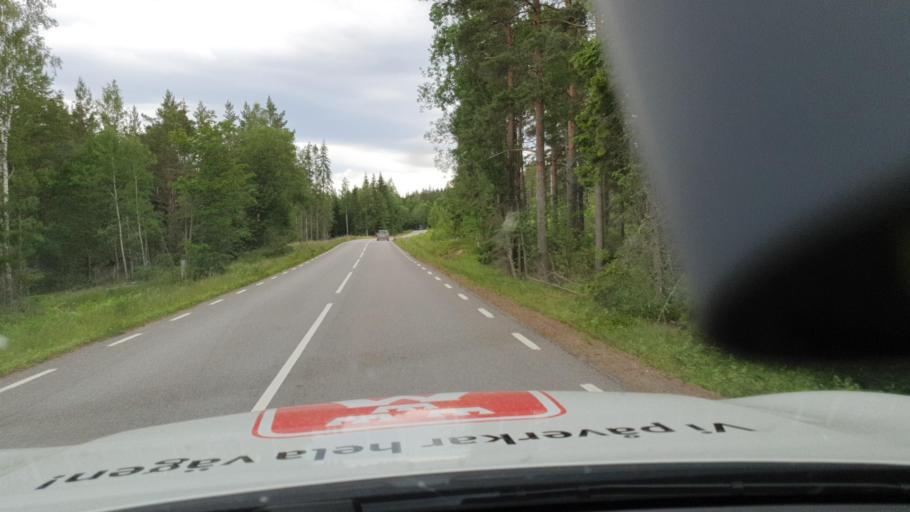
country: SE
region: Vaestra Goetaland
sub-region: Karlsborgs Kommun
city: Karlsborg
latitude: 58.7328
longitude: 14.5034
